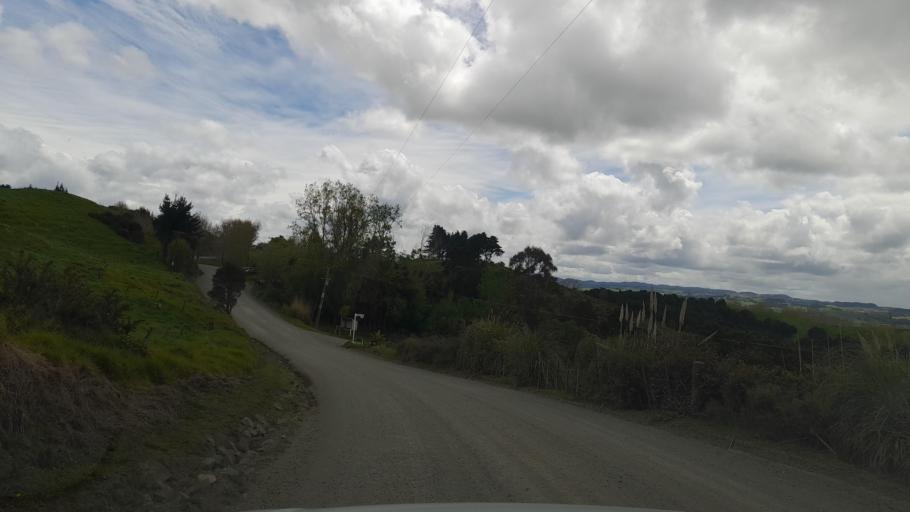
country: NZ
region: Auckland
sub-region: Auckland
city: Wellsford
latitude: -36.1489
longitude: 174.3562
